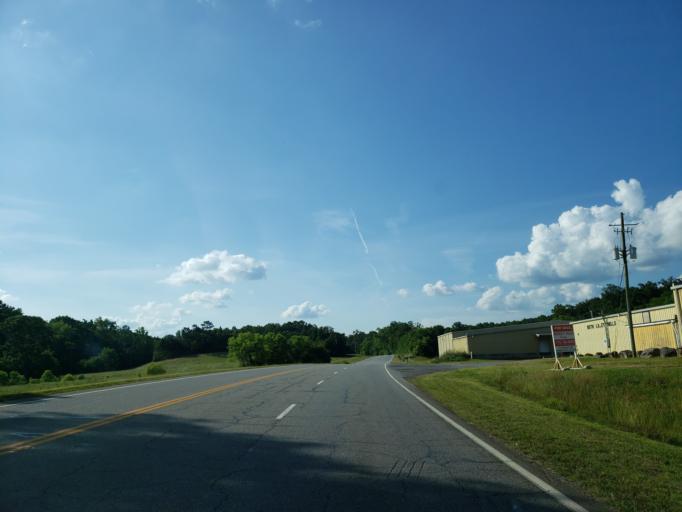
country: US
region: Georgia
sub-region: Bartow County
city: Rydal
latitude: 34.4691
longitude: -84.7023
